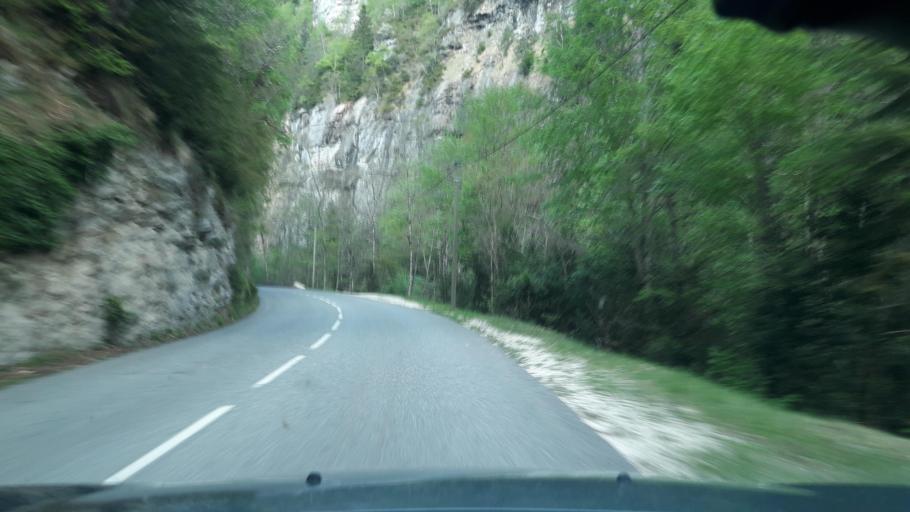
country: FR
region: Rhone-Alpes
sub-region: Departement de la Drome
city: Die
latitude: 44.6821
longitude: 5.5712
